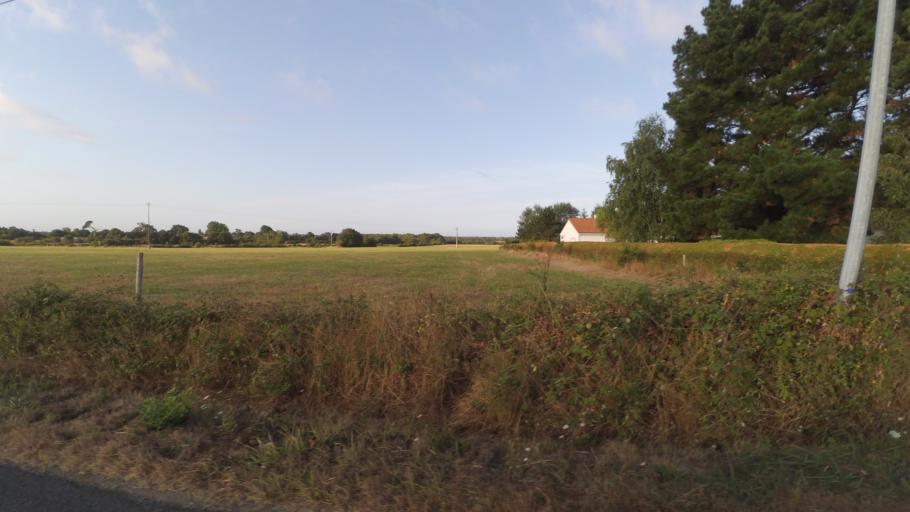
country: FR
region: Pays de la Loire
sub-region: Departement de la Loire-Atlantique
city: Vieillevigne
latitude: 46.9858
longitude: -1.4559
